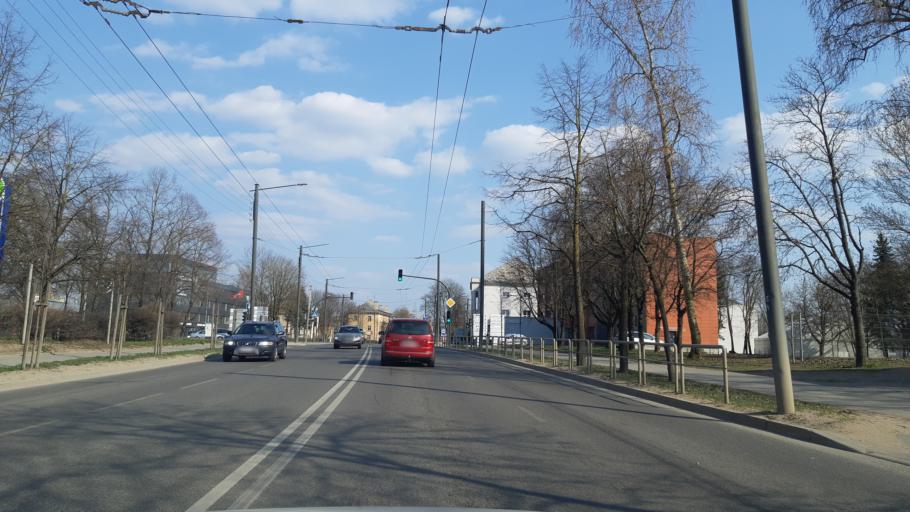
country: LT
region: Kauno apskritis
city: Dainava (Kaunas)
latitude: 54.8948
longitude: 23.9851
